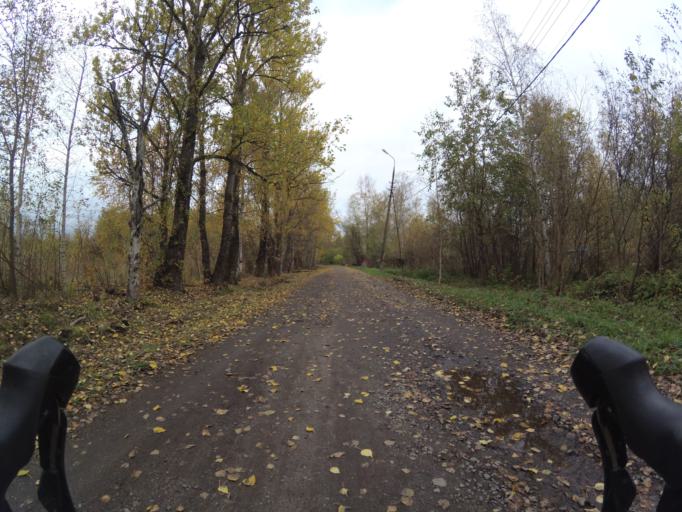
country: RU
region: St.-Petersburg
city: Lakhtinskiy
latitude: 59.9963
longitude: 30.1628
